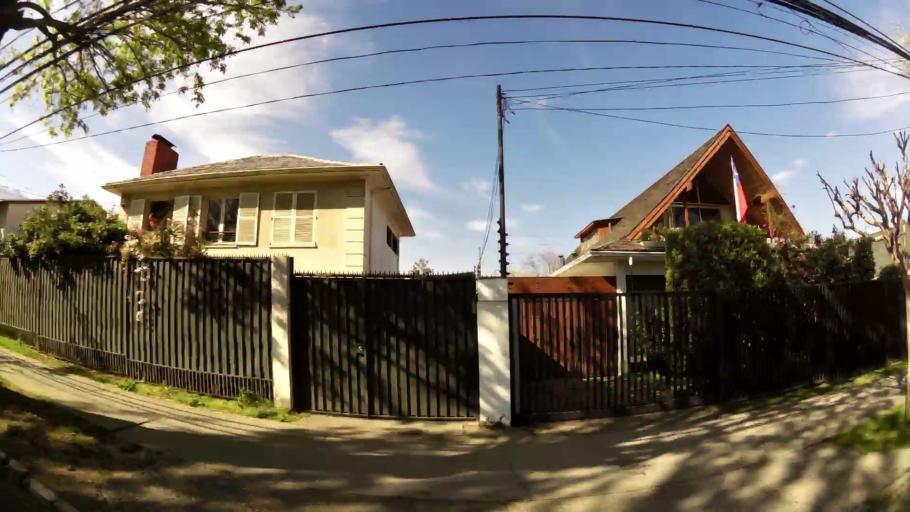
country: CL
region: Santiago Metropolitan
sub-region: Provincia de Santiago
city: Villa Presidente Frei, Nunoa, Santiago, Chile
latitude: -33.4364
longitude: -70.5598
